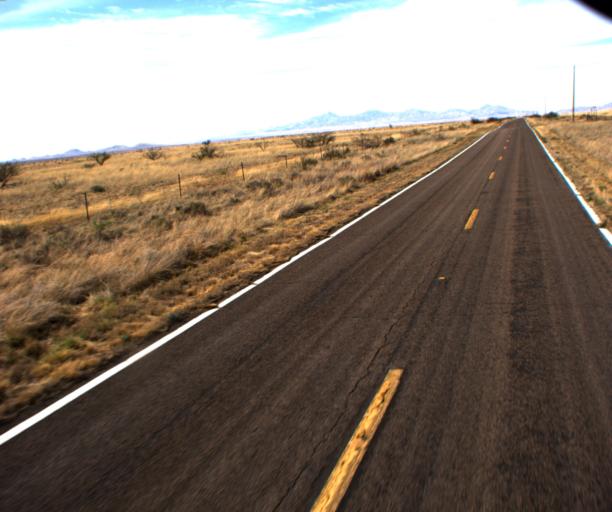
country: US
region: Arizona
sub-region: Cochise County
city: Willcox
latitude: 31.8929
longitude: -109.4913
